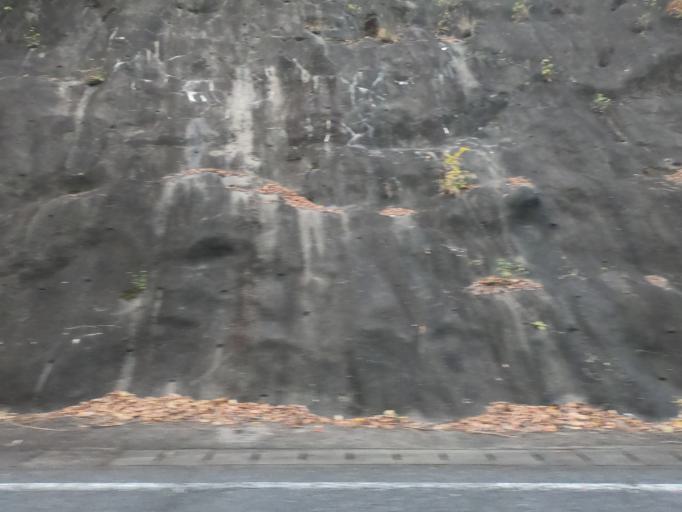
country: JP
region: Kumamoto
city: Minamata
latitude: 32.2562
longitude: 130.5075
